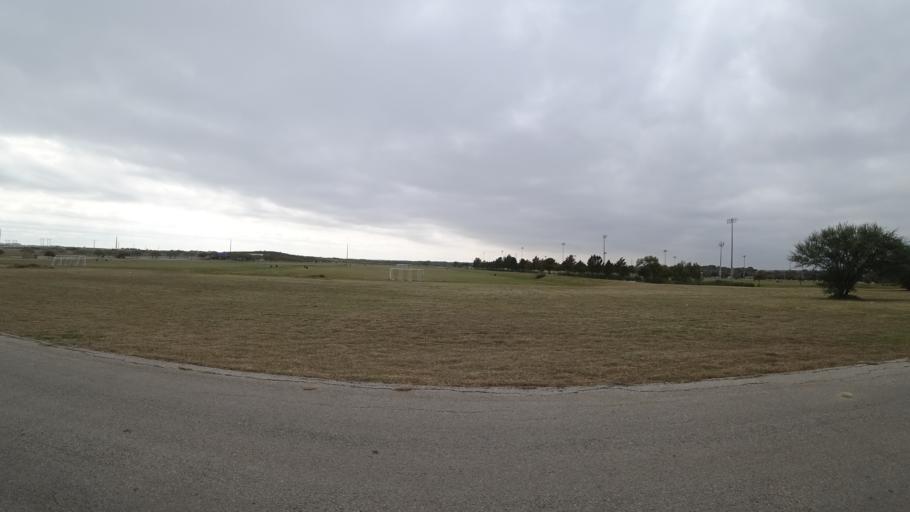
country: US
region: Texas
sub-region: Travis County
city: Pflugerville
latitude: 30.4152
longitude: -97.5944
